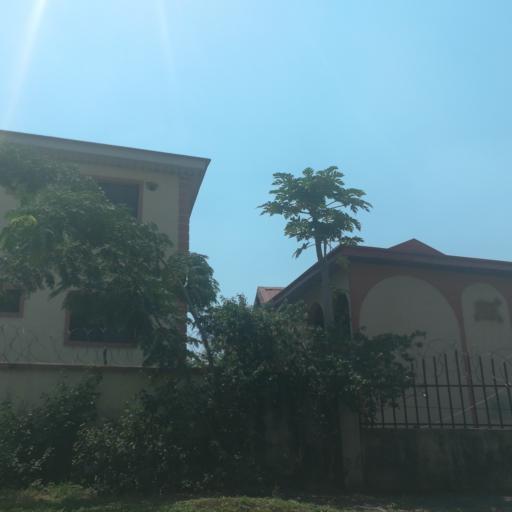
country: NG
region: Abuja Federal Capital Territory
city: Abuja
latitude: 9.0690
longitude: 7.4493
